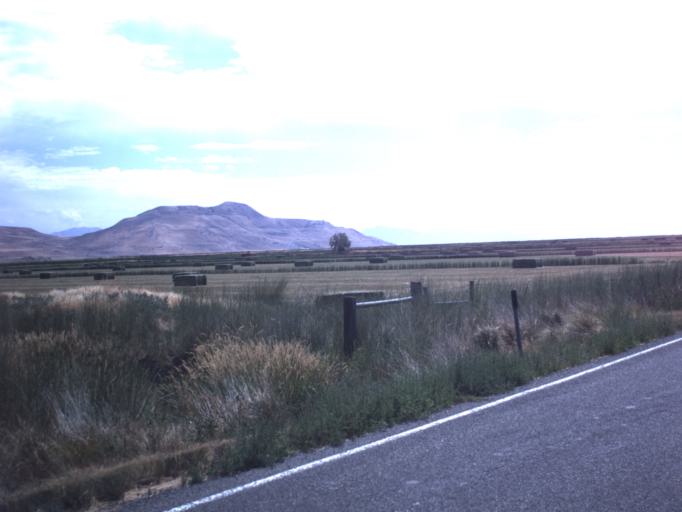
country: US
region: Utah
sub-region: Box Elder County
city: Tremonton
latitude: 41.6435
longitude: -112.3142
